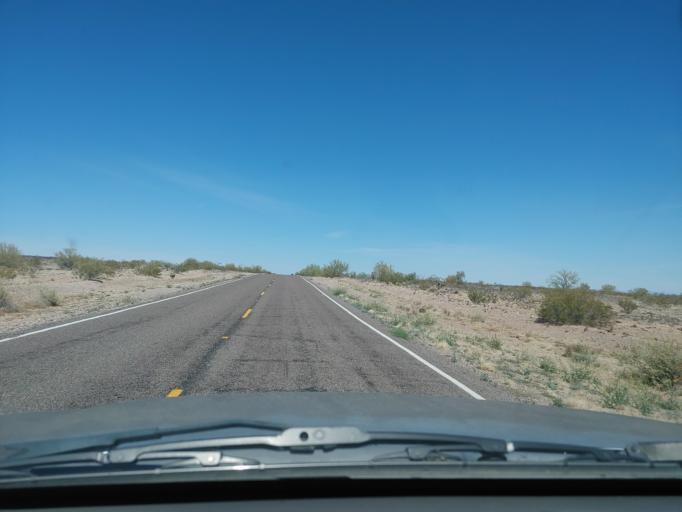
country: US
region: Arizona
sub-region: Maricopa County
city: Gila Bend
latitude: 32.8821
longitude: -113.2285
